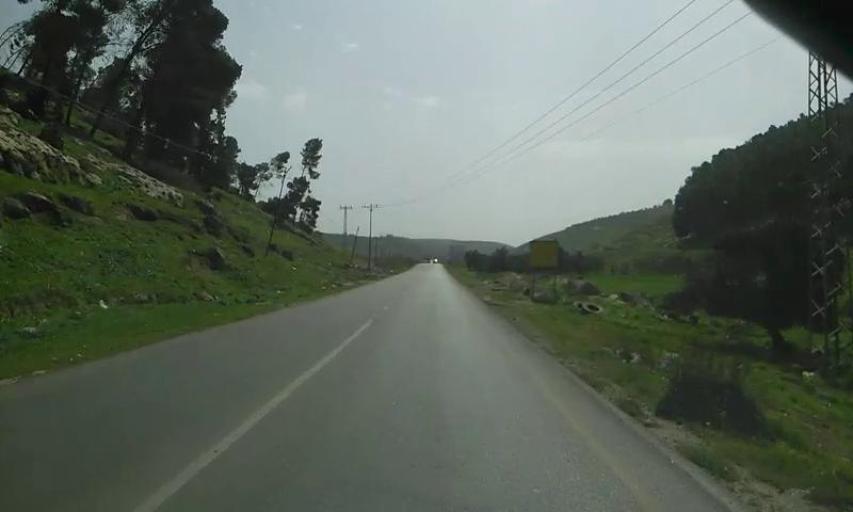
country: PS
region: West Bank
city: Mirkah
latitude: 32.3993
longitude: 35.2239
